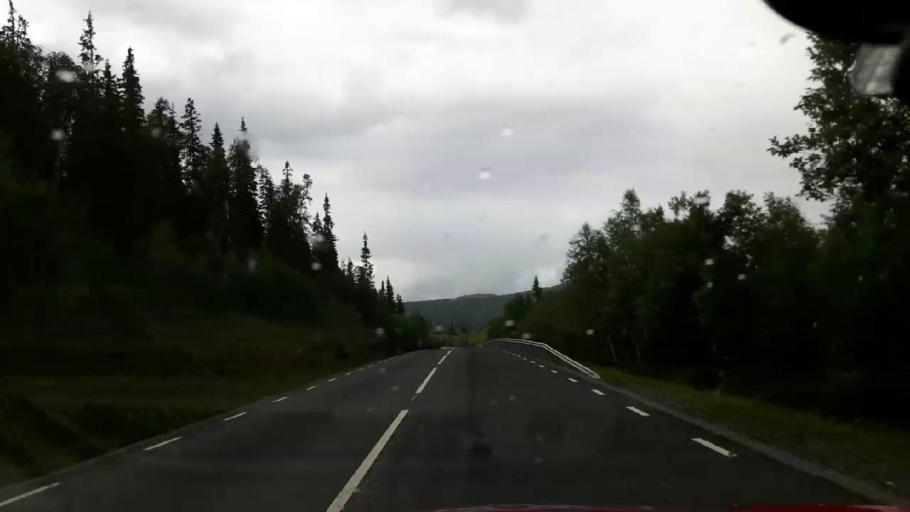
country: NO
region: Nord-Trondelag
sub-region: Royrvik
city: Royrvik
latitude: 64.9041
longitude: 14.1976
